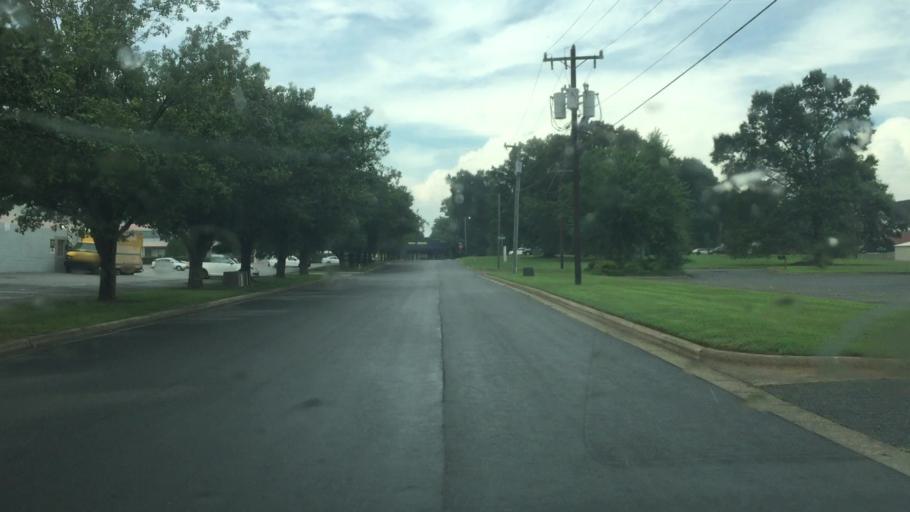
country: US
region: North Carolina
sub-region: Iredell County
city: Mooresville
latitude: 35.5881
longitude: -80.7936
